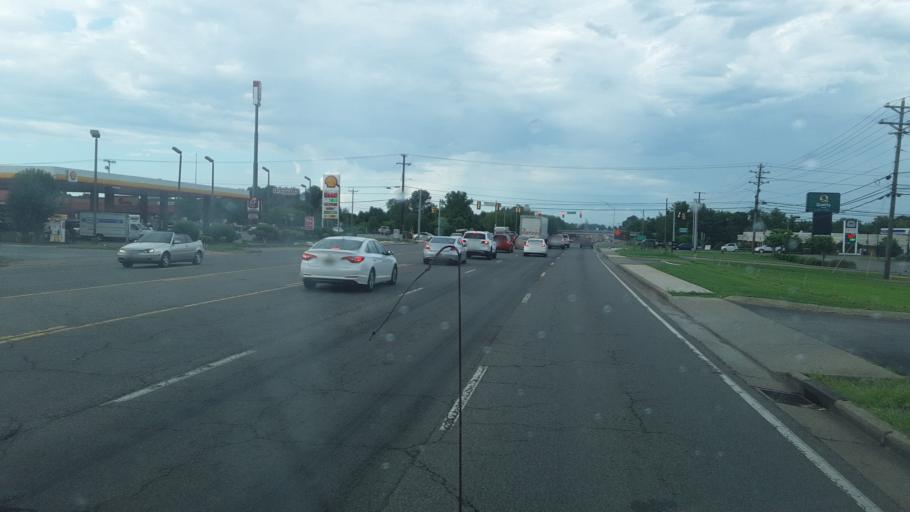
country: US
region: Tennessee
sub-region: Montgomery County
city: Clarksville
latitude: 36.5962
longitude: -87.2864
